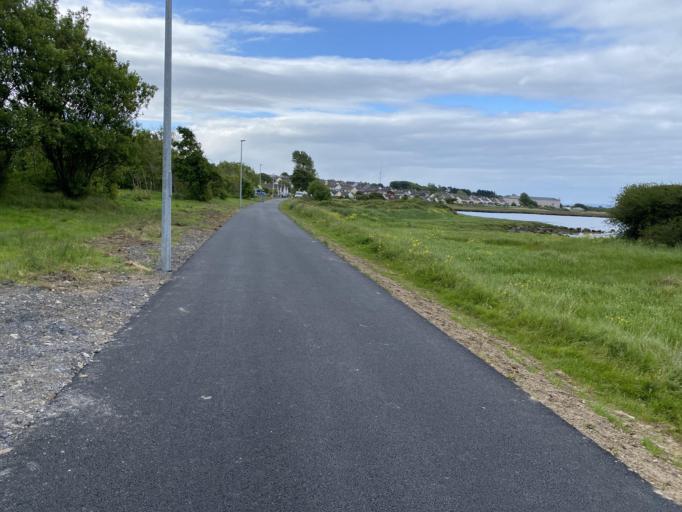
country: IE
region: Connaught
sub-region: County Galway
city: Gaillimh
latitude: 53.2798
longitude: -9.0301
